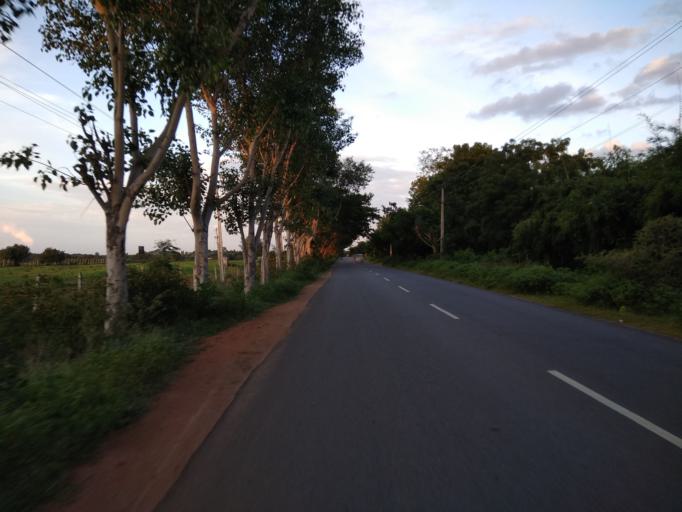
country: IN
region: Telangana
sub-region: Rangareddi
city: Sriramnagar
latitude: 17.2546
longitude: 78.3097
